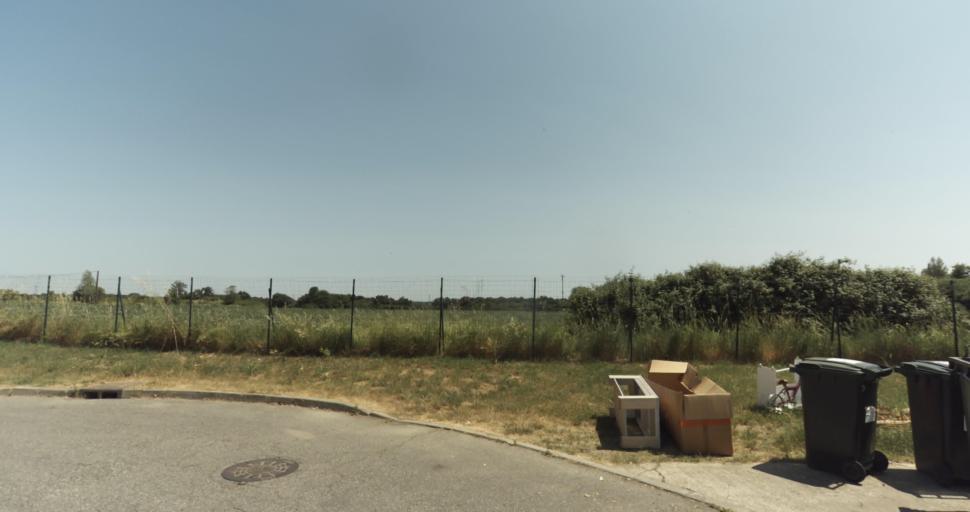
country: FR
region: Midi-Pyrenees
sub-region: Departement de la Haute-Garonne
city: La Salvetat-Saint-Gilles
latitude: 43.6002
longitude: 1.2641
